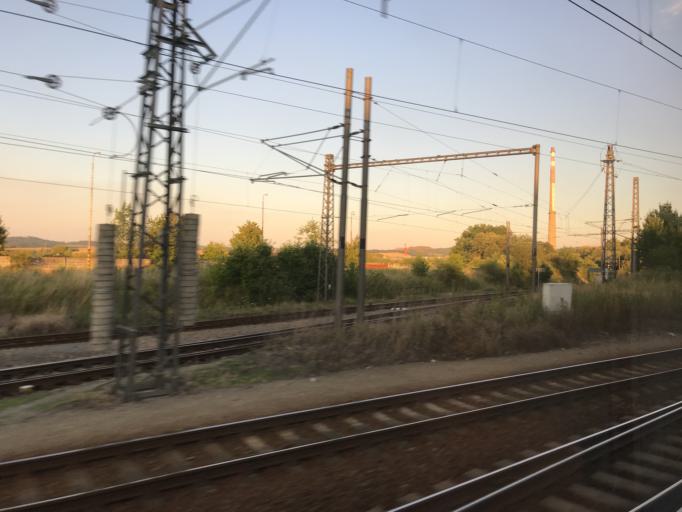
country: CZ
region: Central Bohemia
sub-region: Okres Benesov
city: Benesov
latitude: 49.7736
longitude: 14.6863
